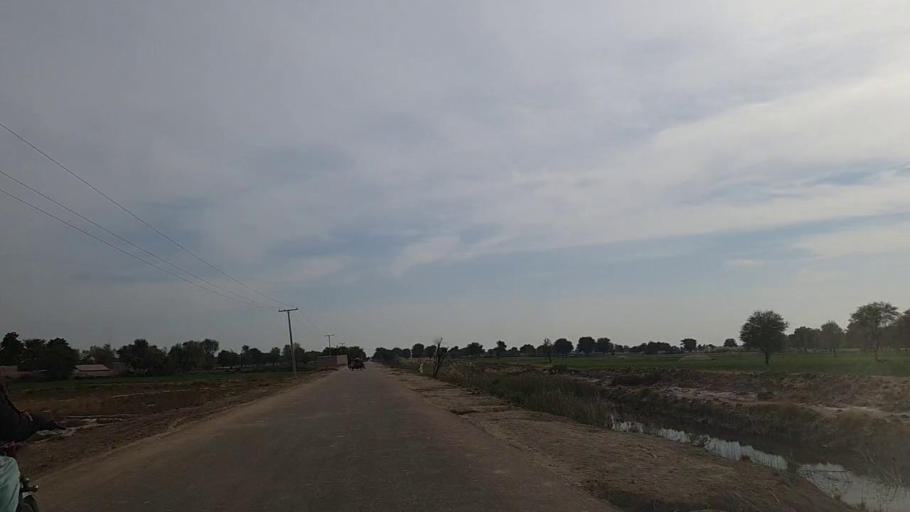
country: PK
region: Sindh
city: Daur
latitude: 26.4203
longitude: 68.4863
